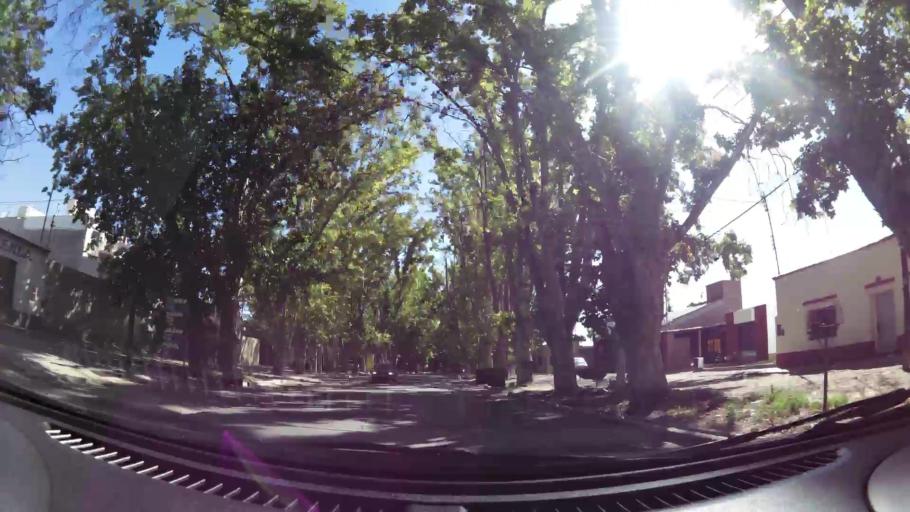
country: AR
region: Mendoza
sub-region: Departamento de Godoy Cruz
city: Godoy Cruz
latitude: -32.9768
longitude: -68.8576
